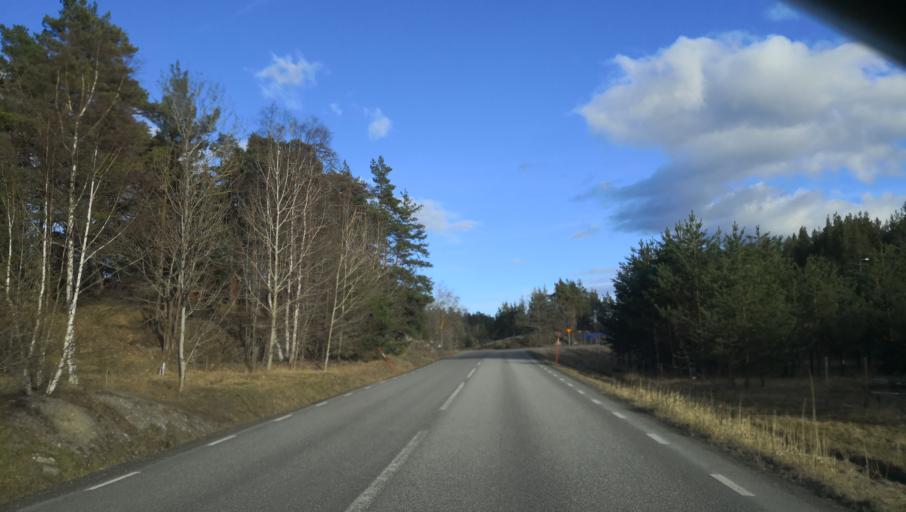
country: SE
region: Stockholm
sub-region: Varmdo Kommun
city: Gustavsberg
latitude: 59.3477
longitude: 18.3813
